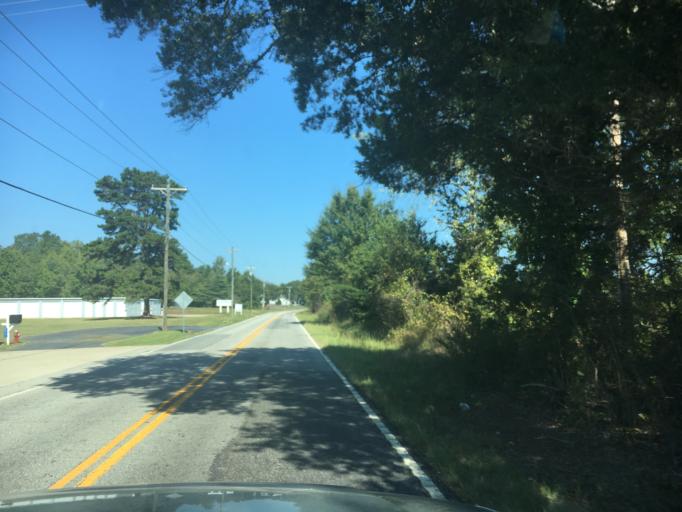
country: US
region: South Carolina
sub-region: Spartanburg County
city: Inman
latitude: 35.1214
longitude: -82.0438
